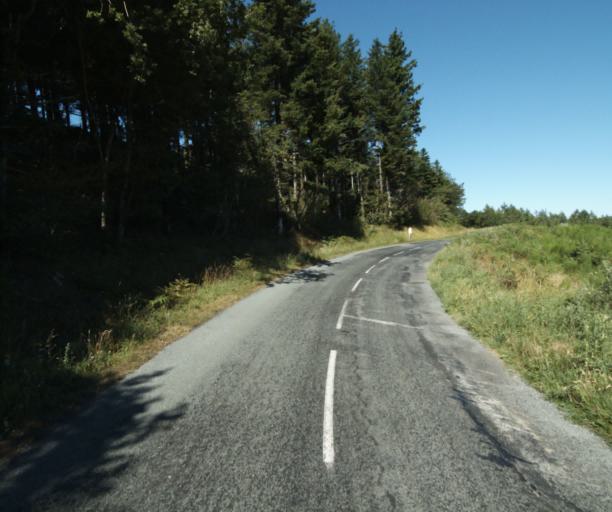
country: FR
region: Midi-Pyrenees
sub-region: Departement du Tarn
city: Dourgne
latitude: 43.4392
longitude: 2.1395
